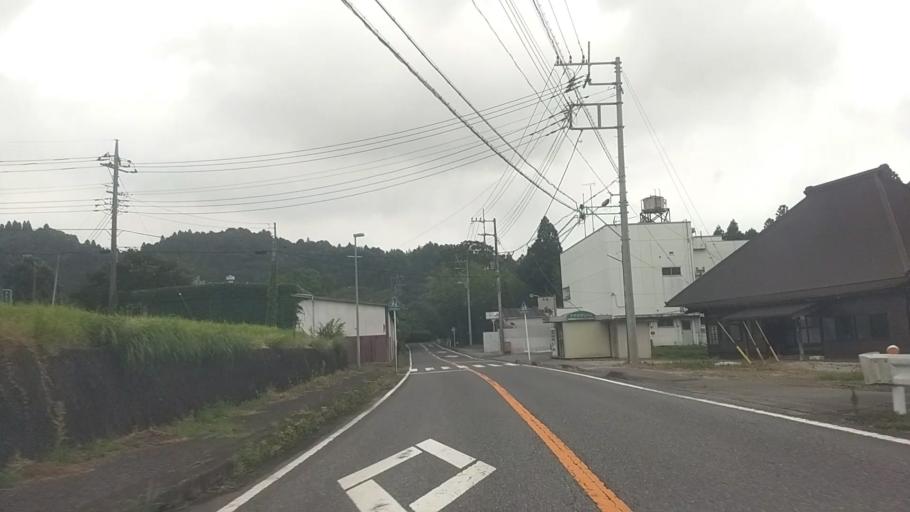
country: JP
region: Chiba
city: Katsuura
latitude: 35.2521
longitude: 140.2196
